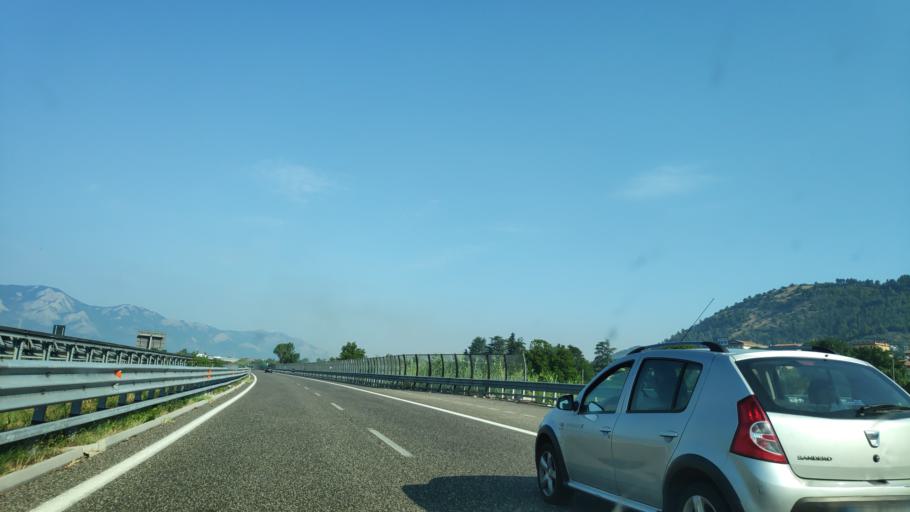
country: IT
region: Campania
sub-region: Provincia di Salerno
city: Sala Consilina
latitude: 40.4025
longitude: 15.5772
